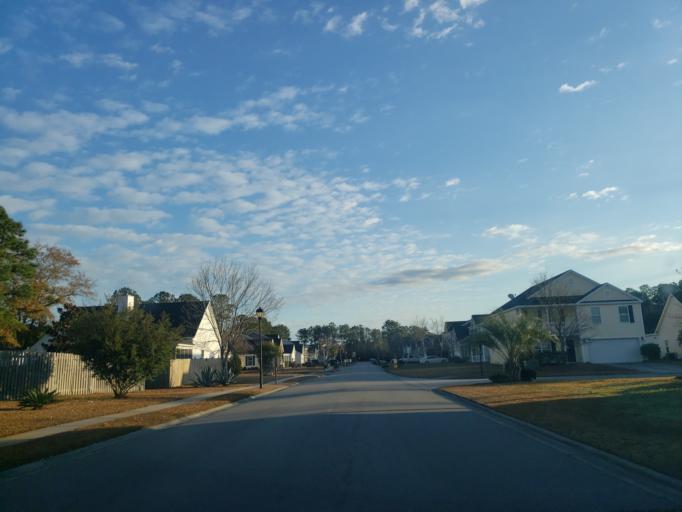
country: US
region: Georgia
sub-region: Chatham County
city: Bloomingdale
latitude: 32.1558
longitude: -81.2686
